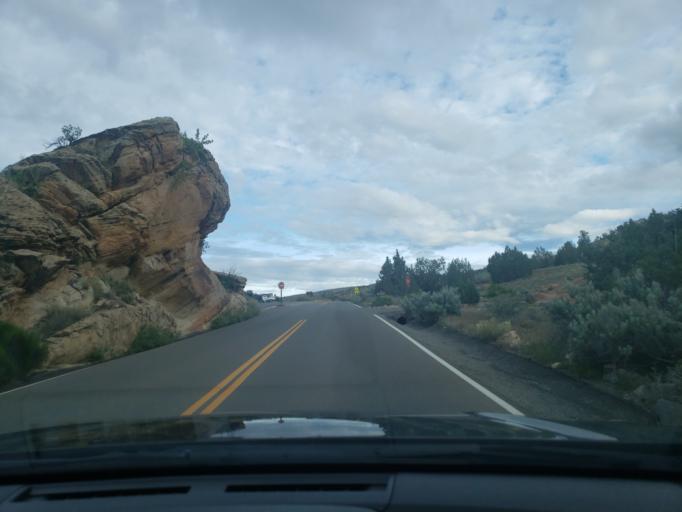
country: US
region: Colorado
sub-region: Mesa County
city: Redlands
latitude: 39.0326
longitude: -108.6314
